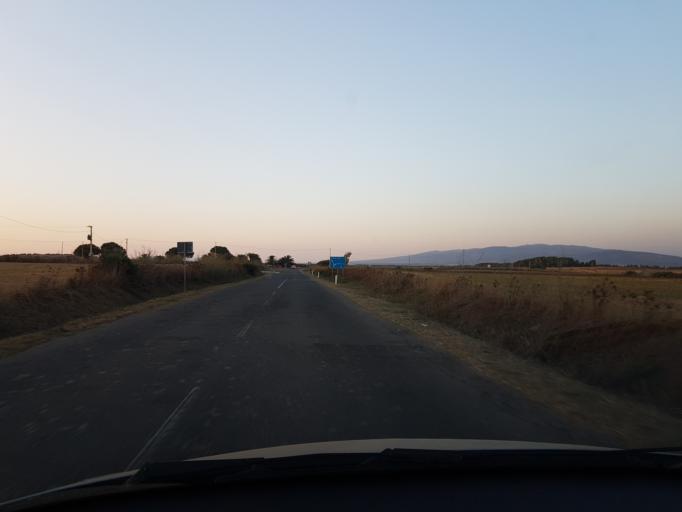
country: IT
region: Sardinia
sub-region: Provincia di Oristano
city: Nurachi
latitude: 39.9827
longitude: 8.4546
